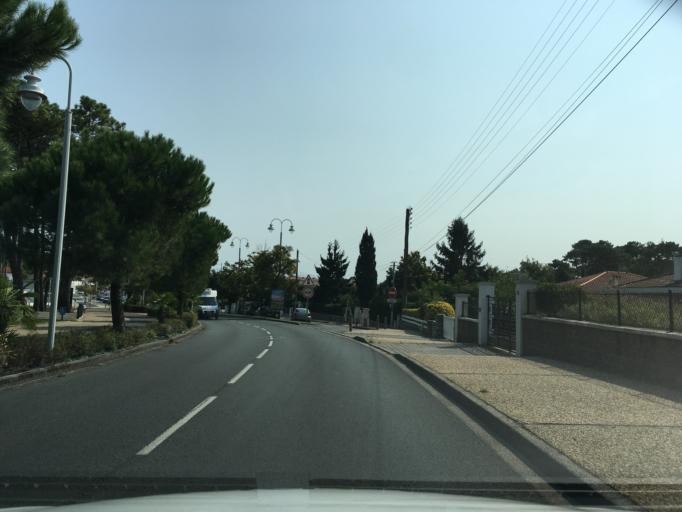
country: FR
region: Aquitaine
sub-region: Departement des Pyrenees-Atlantiques
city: Boucau
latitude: 43.5220
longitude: -1.5035
